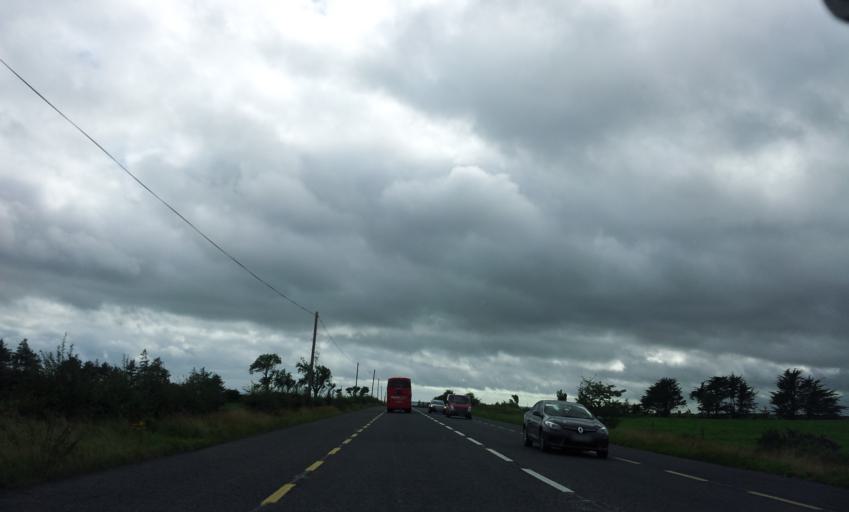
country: IE
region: Munster
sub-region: Waterford
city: Dungarvan
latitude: 52.0003
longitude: -7.7242
